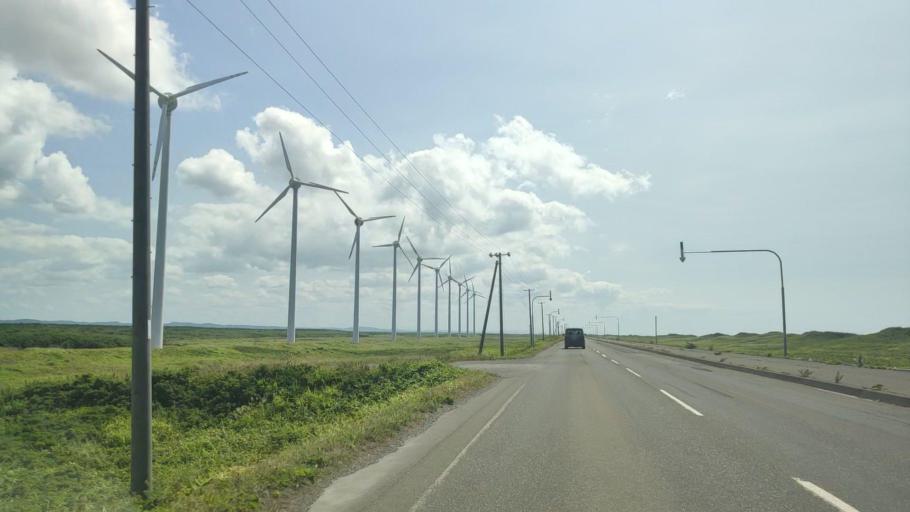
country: JP
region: Hokkaido
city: Makubetsu
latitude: 44.9675
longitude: 141.7012
